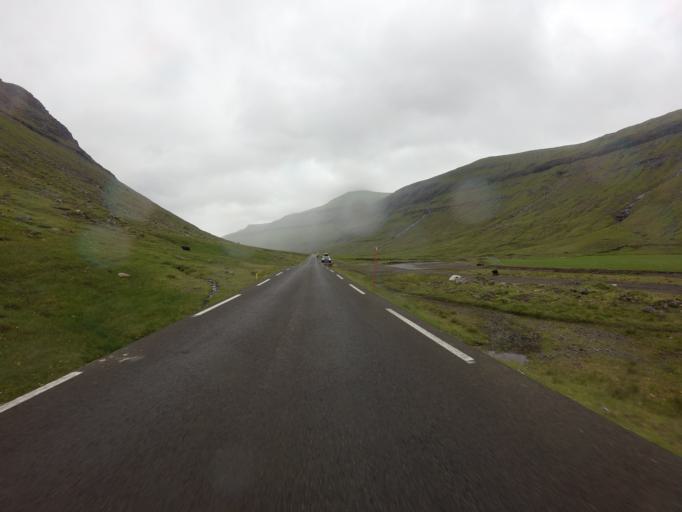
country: FO
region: Streymoy
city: Vestmanna
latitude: 62.2292
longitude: -7.1354
